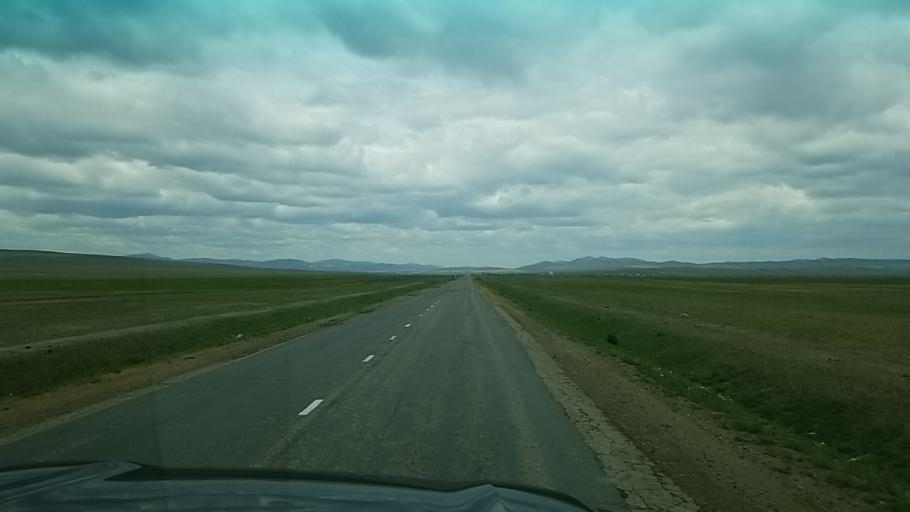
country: MN
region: Darhan Uul
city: Hongor
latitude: 49.2552
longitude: 105.9984
